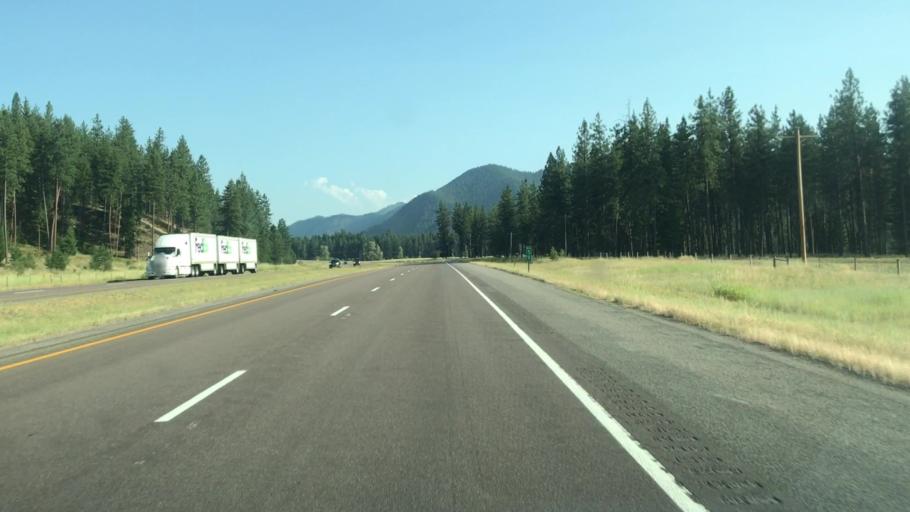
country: US
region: Montana
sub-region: Mineral County
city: Superior
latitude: 47.0624
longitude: -114.7637
